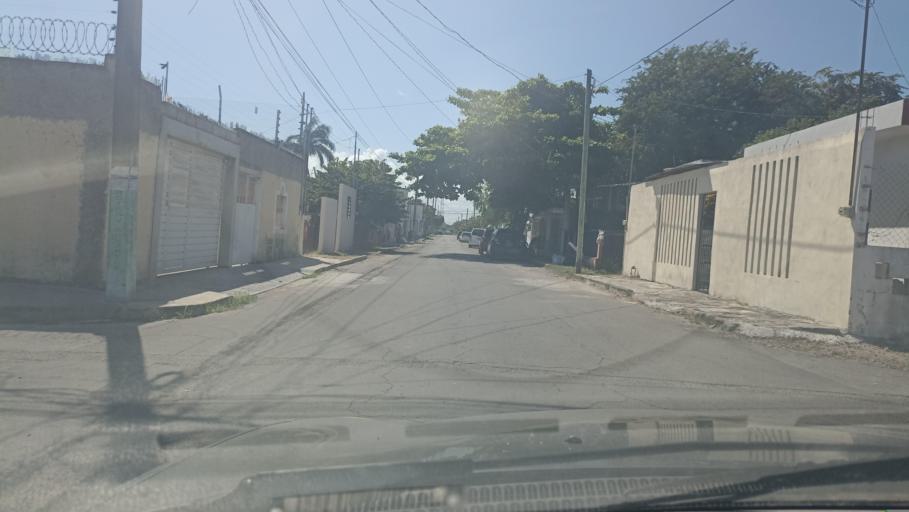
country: MX
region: Quintana Roo
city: Chetumal
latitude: 18.5152
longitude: -88.2859
